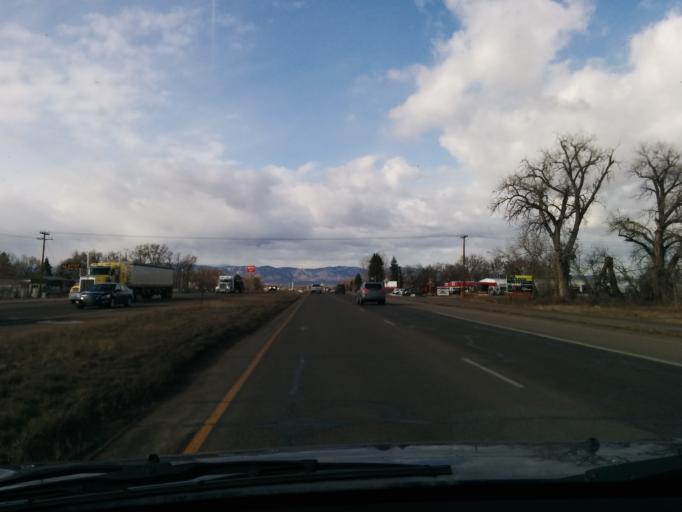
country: US
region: Colorado
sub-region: Larimer County
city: Fort Collins
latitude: 40.5813
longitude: -105.0189
